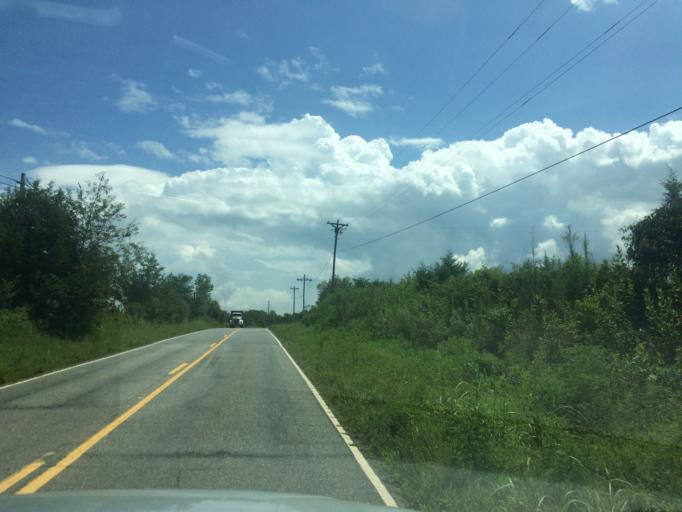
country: US
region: North Carolina
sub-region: Polk County
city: Columbus
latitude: 35.2857
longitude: -82.1196
